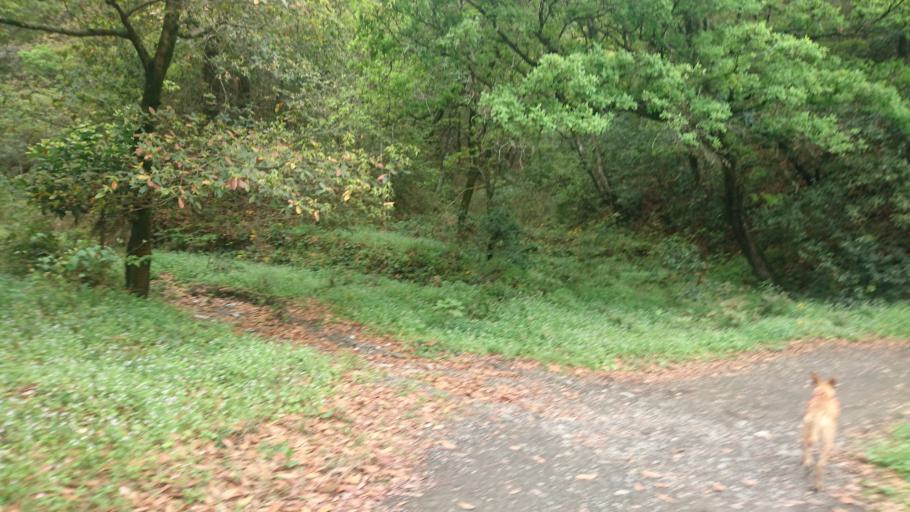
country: MX
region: Nuevo Leon
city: Garza Garcia
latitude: 25.6040
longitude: -100.3415
